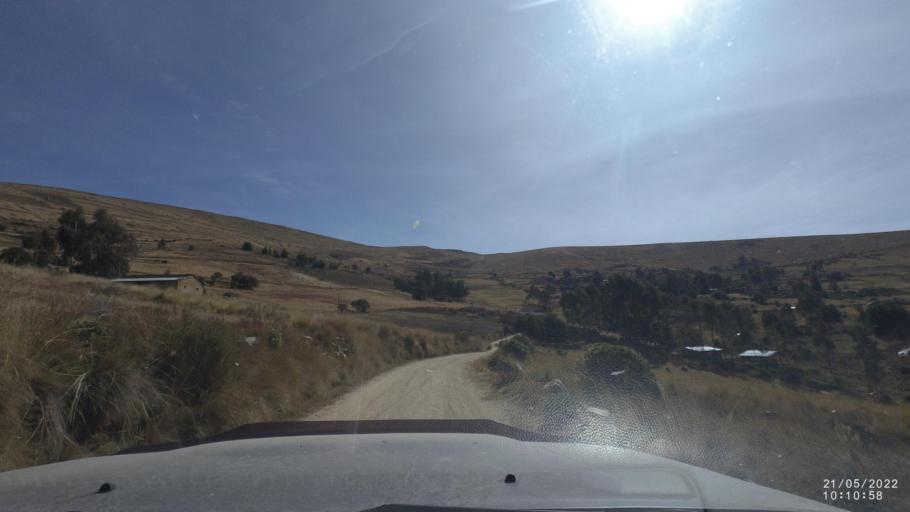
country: BO
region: Cochabamba
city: Colomi
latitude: -17.3334
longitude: -65.9819
